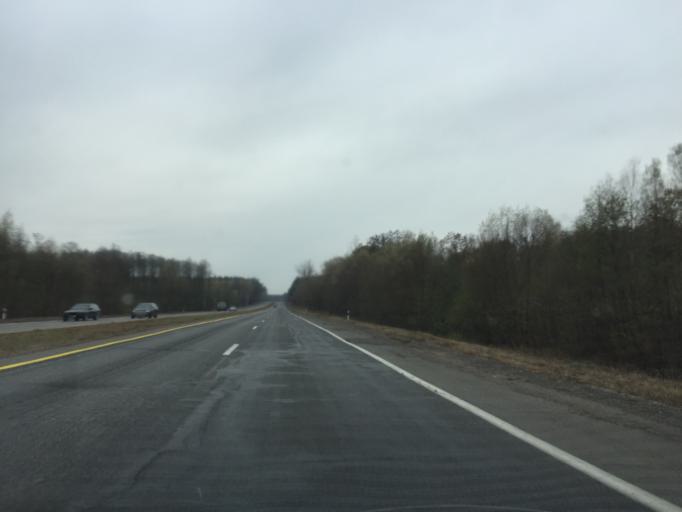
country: BY
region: Gomel
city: Horad Rechytsa
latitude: 52.3581
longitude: 30.6758
